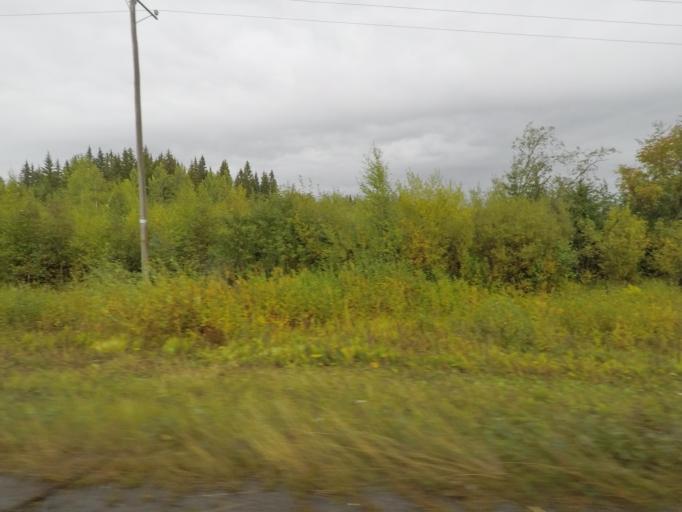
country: FI
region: Southern Savonia
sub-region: Pieksaemaeki
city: Juva
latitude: 61.9334
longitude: 27.8060
